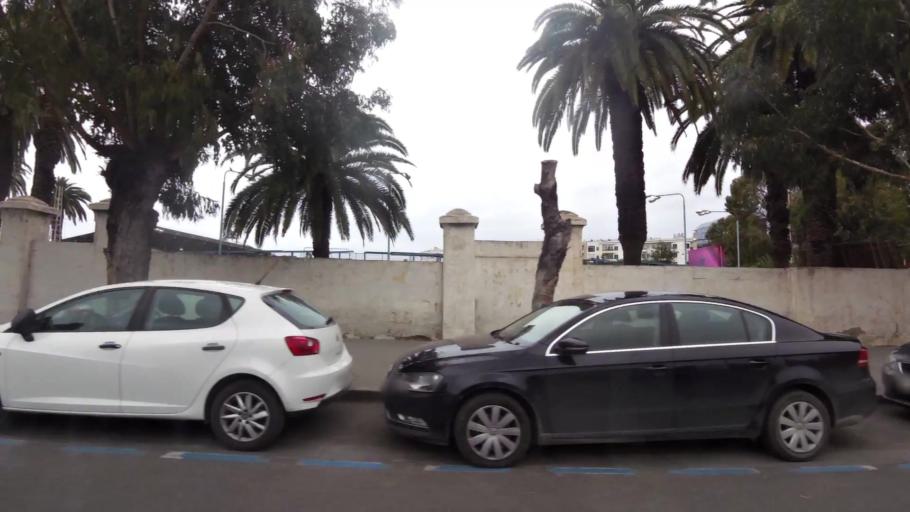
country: MA
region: Grand Casablanca
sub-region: Casablanca
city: Casablanca
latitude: 33.5885
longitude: -7.6459
